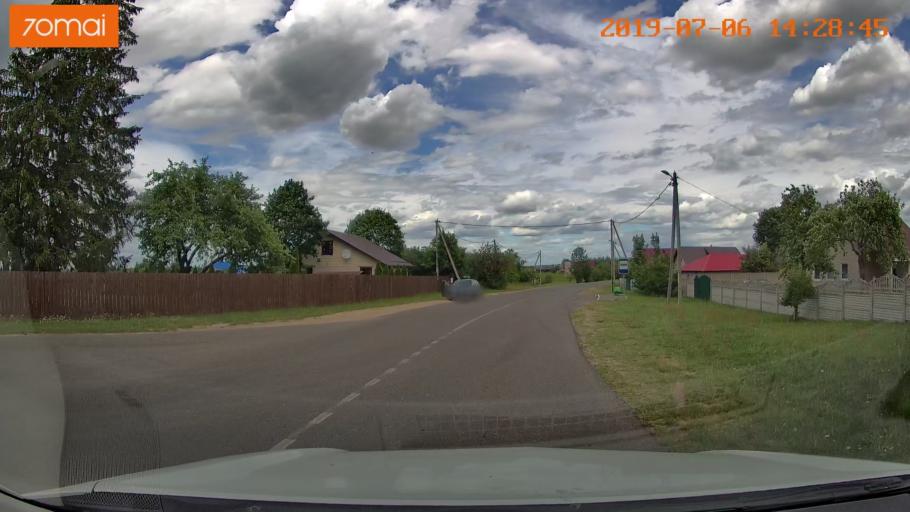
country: BY
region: Minsk
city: Ivyanyets
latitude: 53.9395
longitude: 26.7998
